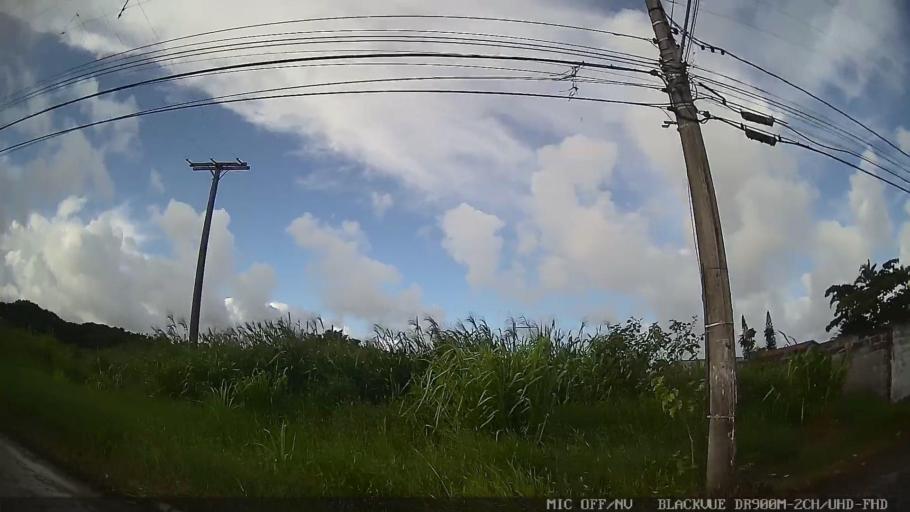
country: BR
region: Sao Paulo
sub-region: Itanhaem
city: Itanhaem
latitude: -24.2009
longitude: -46.8363
